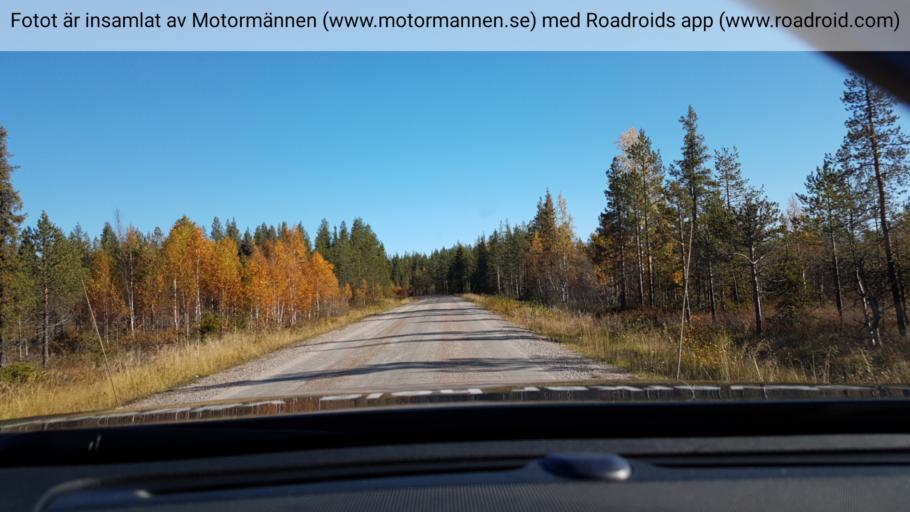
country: SE
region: Norrbotten
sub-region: Gallivare Kommun
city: Gaellivare
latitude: 66.5708
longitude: 21.0413
